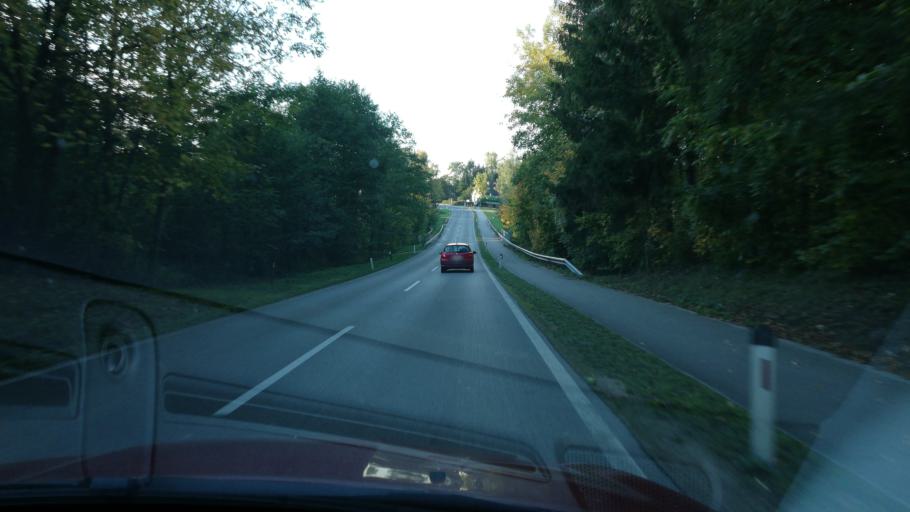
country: AT
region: Upper Austria
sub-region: Politischer Bezirk Steyr-Land
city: Waldneukirchen
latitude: 48.0166
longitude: 14.2402
